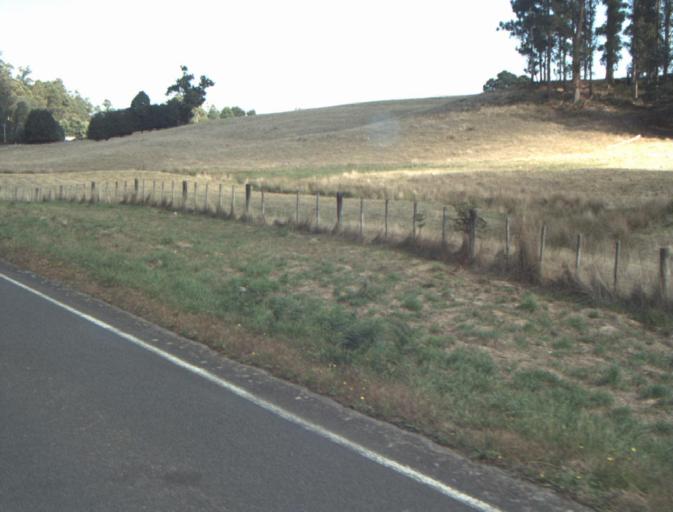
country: AU
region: Tasmania
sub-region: Launceston
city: Mayfield
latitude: -41.2771
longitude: 147.2198
